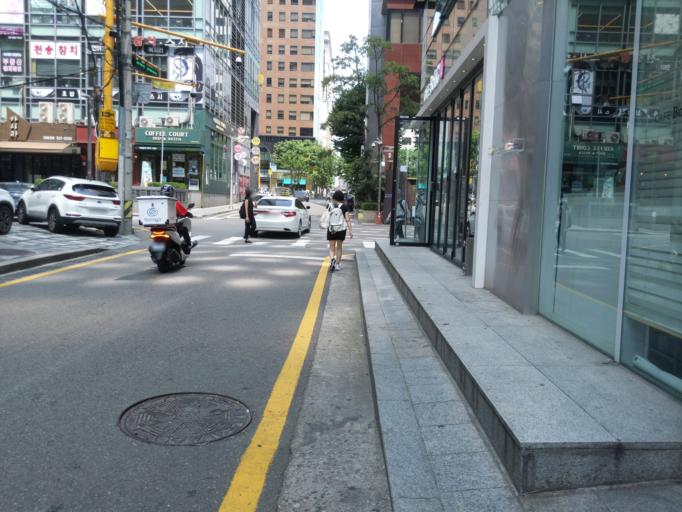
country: KR
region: Seoul
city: Seoul
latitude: 37.4943
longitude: 127.0282
